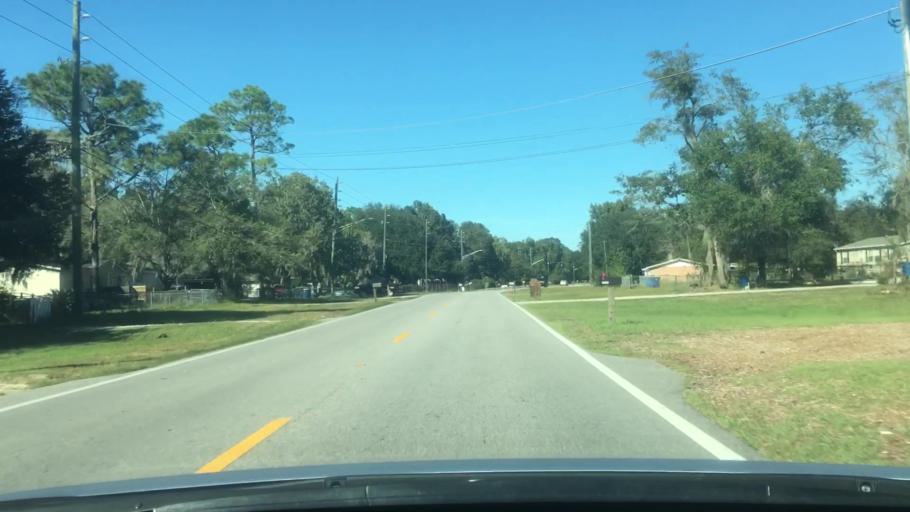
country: US
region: Florida
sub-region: Nassau County
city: Yulee
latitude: 30.4798
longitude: -81.5772
